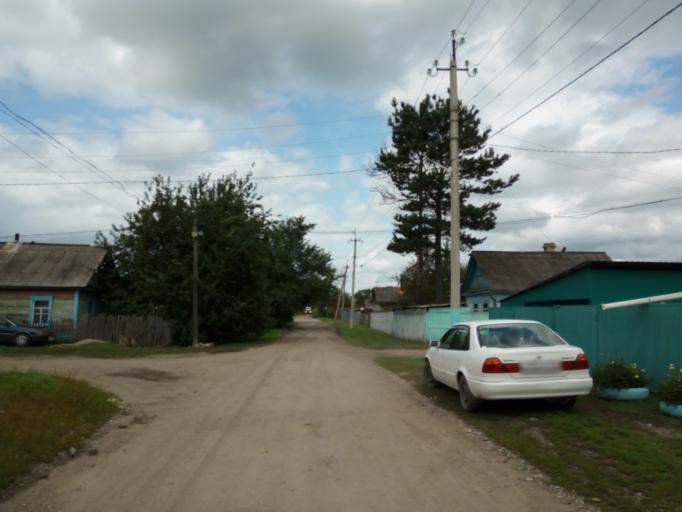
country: RU
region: Primorskiy
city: Dal'nerechensk
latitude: 45.9352
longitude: 133.8124
